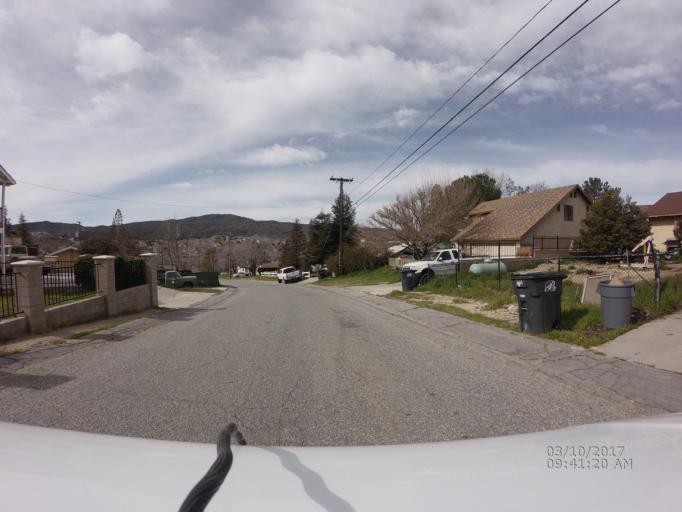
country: US
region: California
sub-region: Los Angeles County
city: Green Valley
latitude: 34.6672
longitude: -118.3891
